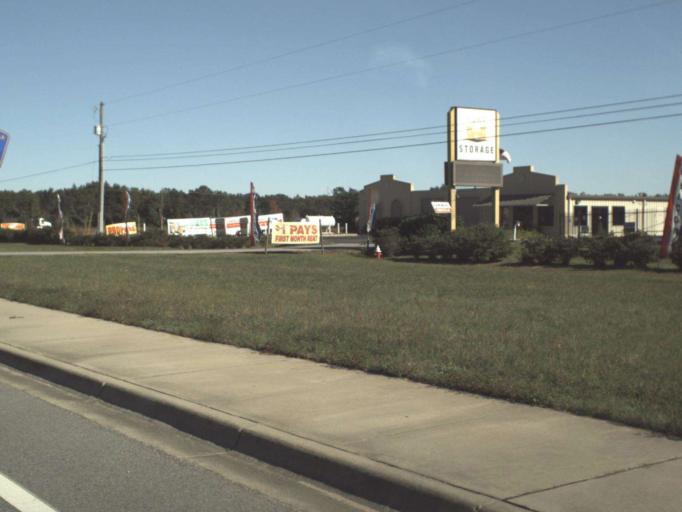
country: US
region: Florida
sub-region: Santa Rosa County
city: Bagdad
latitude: 30.5847
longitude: -87.0859
